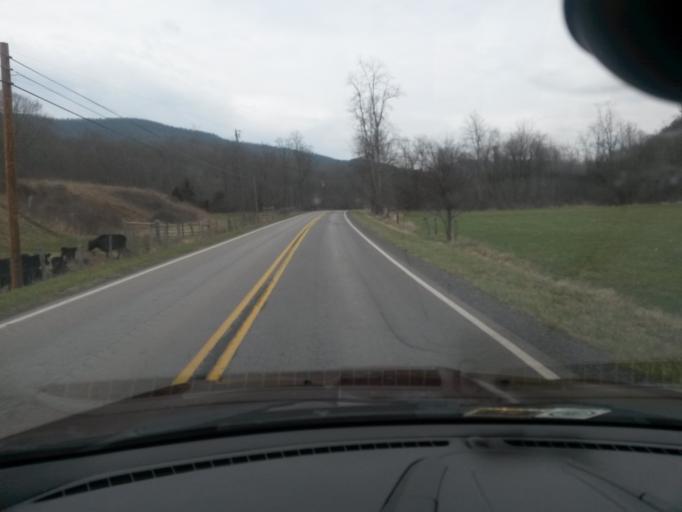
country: US
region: Virginia
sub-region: Highland County
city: Monterey
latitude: 38.3422
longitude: -79.6346
